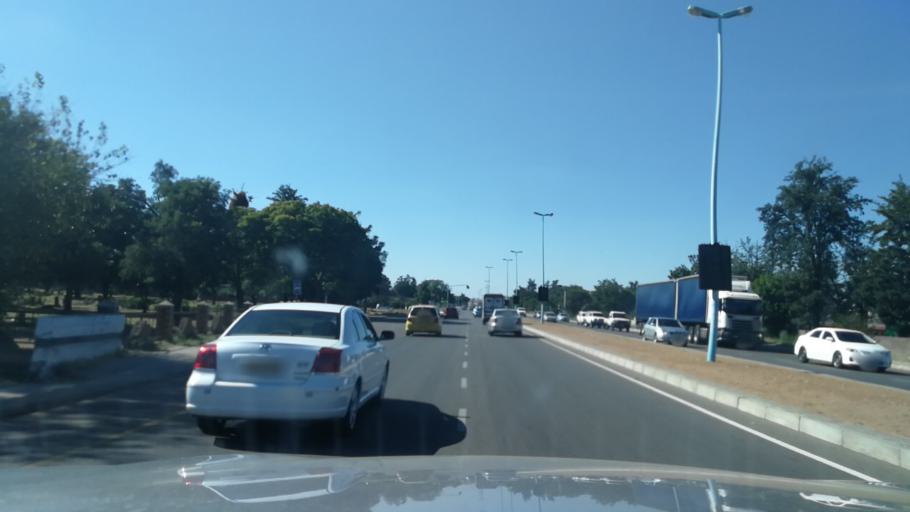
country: BW
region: South East
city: Gaborone
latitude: -24.6768
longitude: 25.9202
